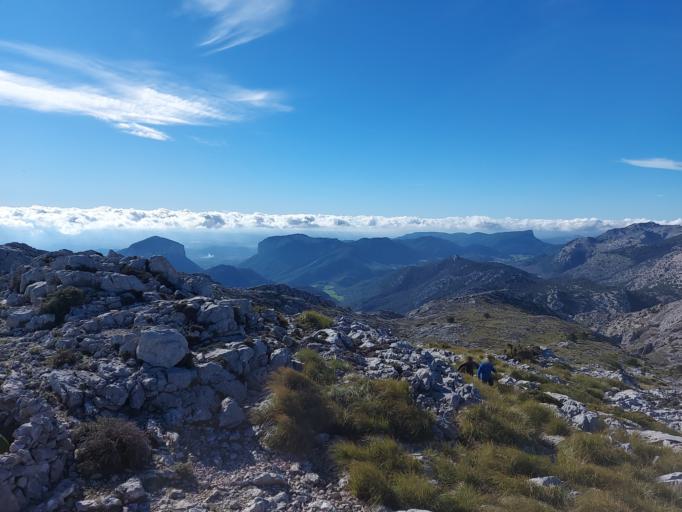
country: ES
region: Balearic Islands
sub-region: Illes Balears
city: Escorca
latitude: 39.7842
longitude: 2.8204
